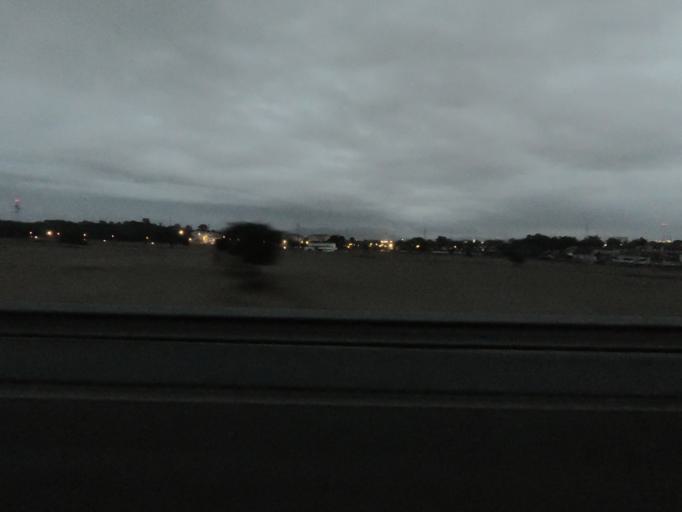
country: PT
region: Setubal
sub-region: Barreiro
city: Santo Antonio da Charneca
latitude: 38.5982
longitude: -9.0429
